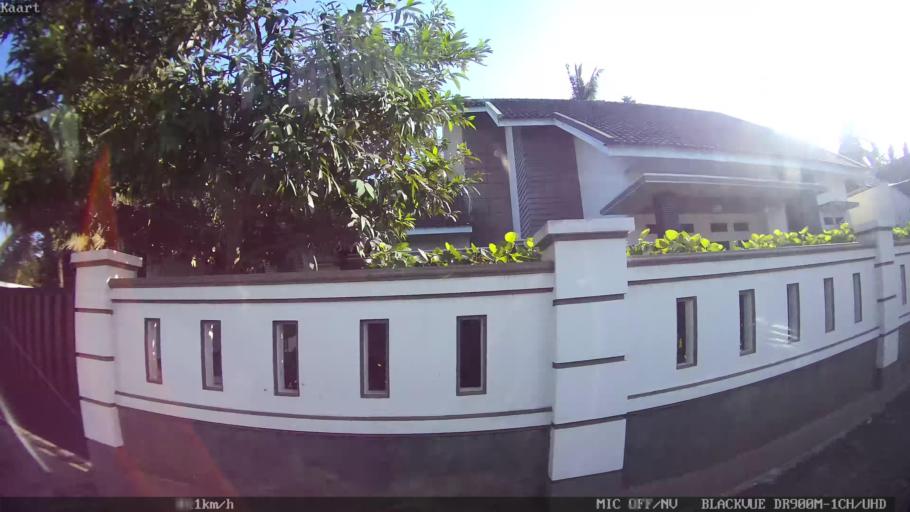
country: ID
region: Lampung
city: Kedaton
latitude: -5.3738
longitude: 105.2296
